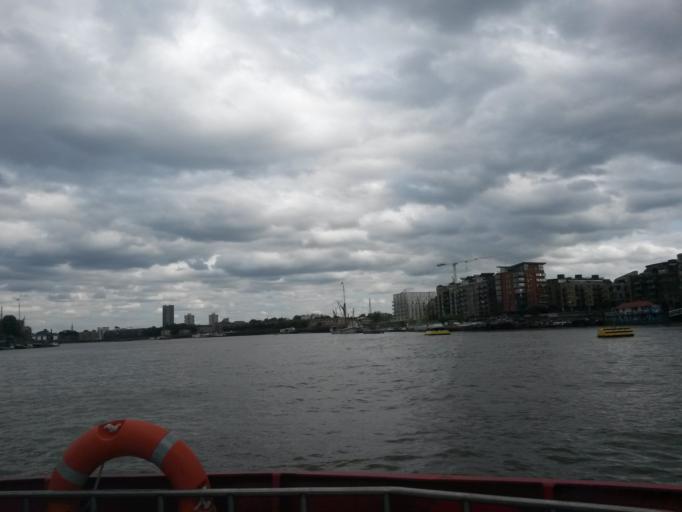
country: GB
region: England
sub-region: Greater London
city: City of London
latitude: 51.5041
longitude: -0.0712
